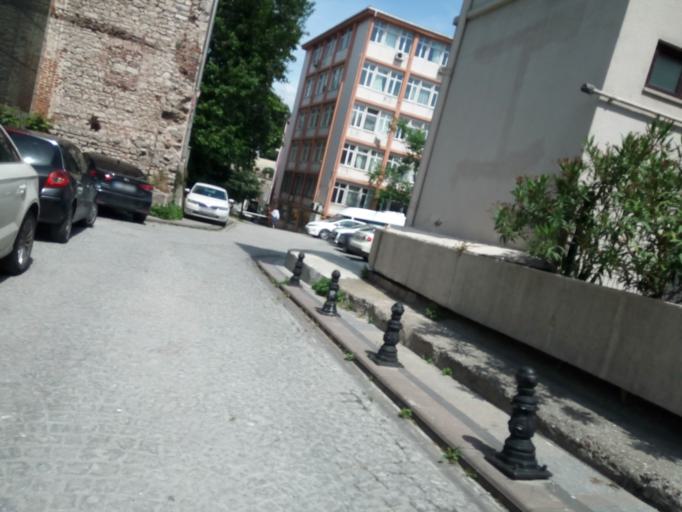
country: TR
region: Istanbul
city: Eminoenue
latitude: 41.0110
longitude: 28.9757
